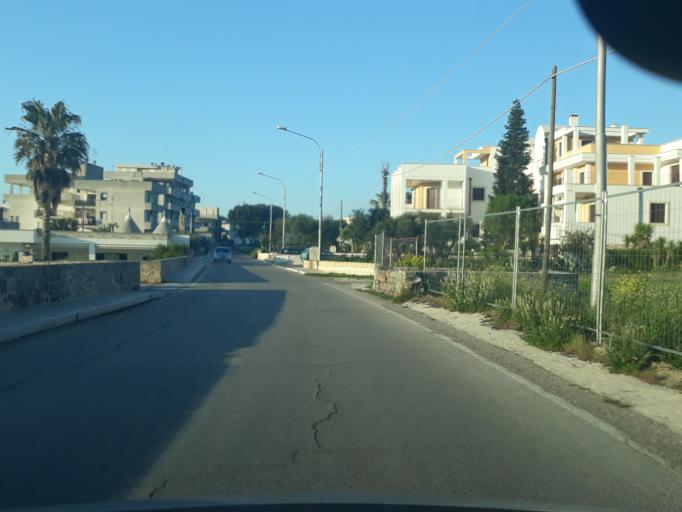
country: IT
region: Apulia
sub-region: Provincia di Bari
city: Locorotondo
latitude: 40.7560
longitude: 17.3308
